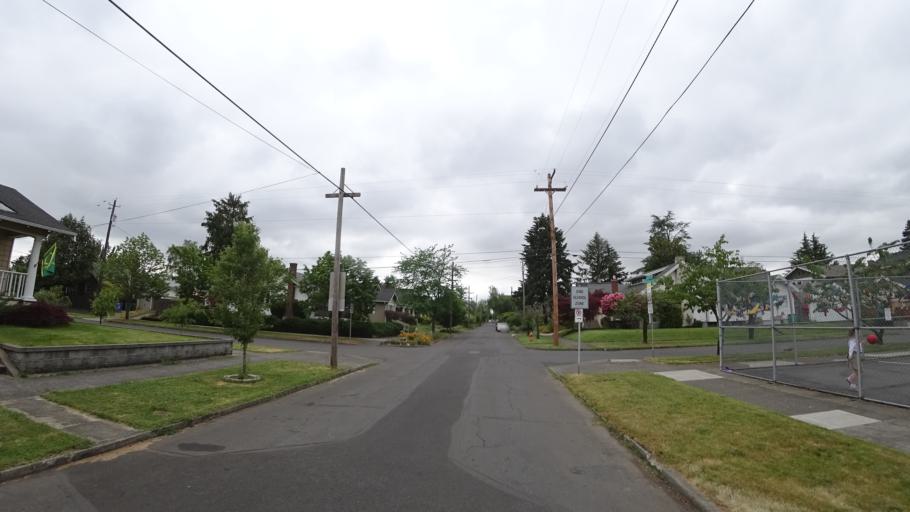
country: US
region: Oregon
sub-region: Multnomah County
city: Portland
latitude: 45.5435
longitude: -122.6087
